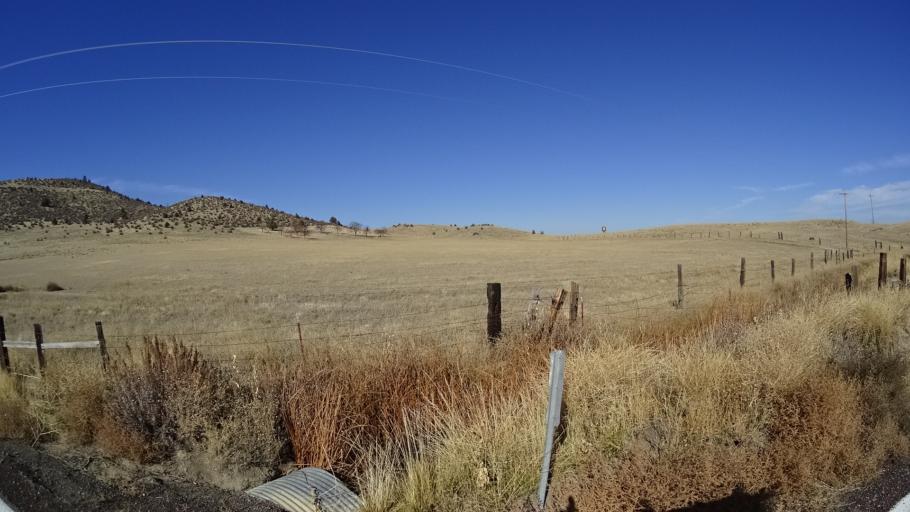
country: US
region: California
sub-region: Siskiyou County
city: Weed
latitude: 41.5107
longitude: -122.5281
